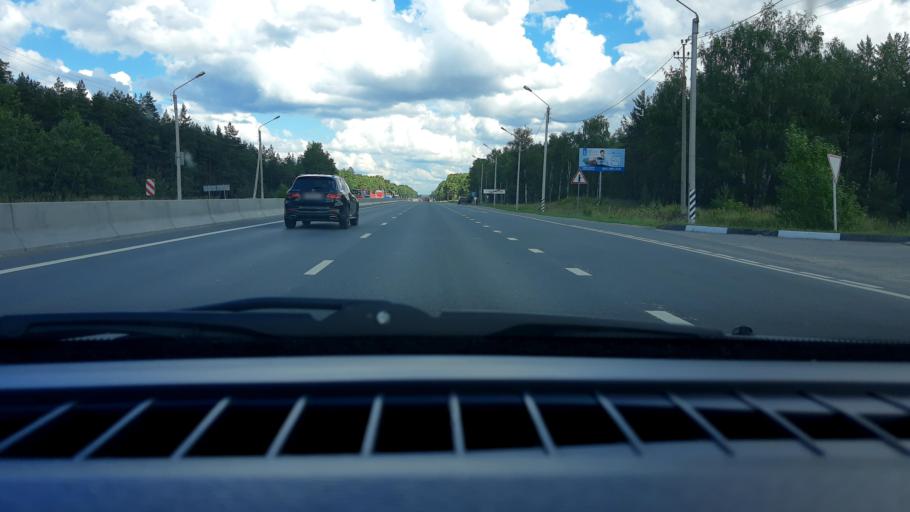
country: RU
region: Nizjnij Novgorod
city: Gorbatovka
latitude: 56.3080
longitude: 43.7029
